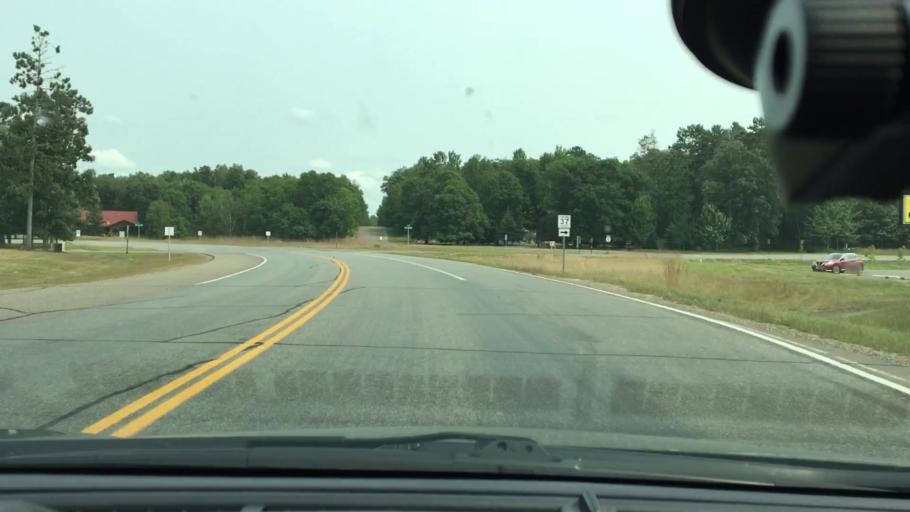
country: US
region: Minnesota
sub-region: Crow Wing County
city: Cross Lake
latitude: 46.6682
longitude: -94.1053
